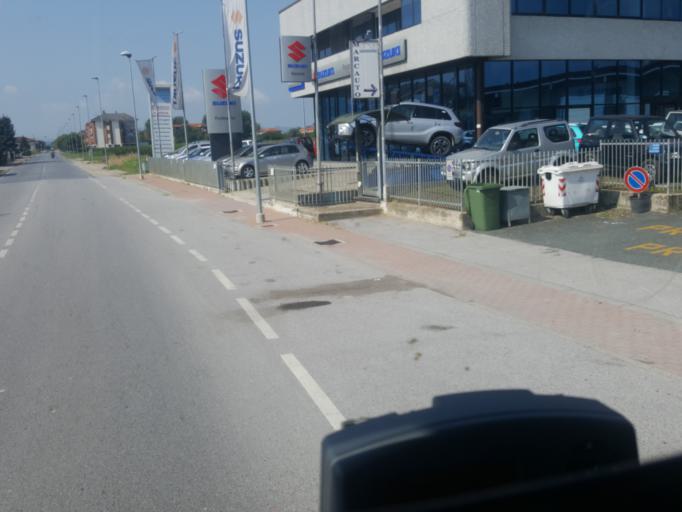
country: IT
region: Piedmont
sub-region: Provincia di Cuneo
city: Vaccheria
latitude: 44.7332
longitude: 8.0488
